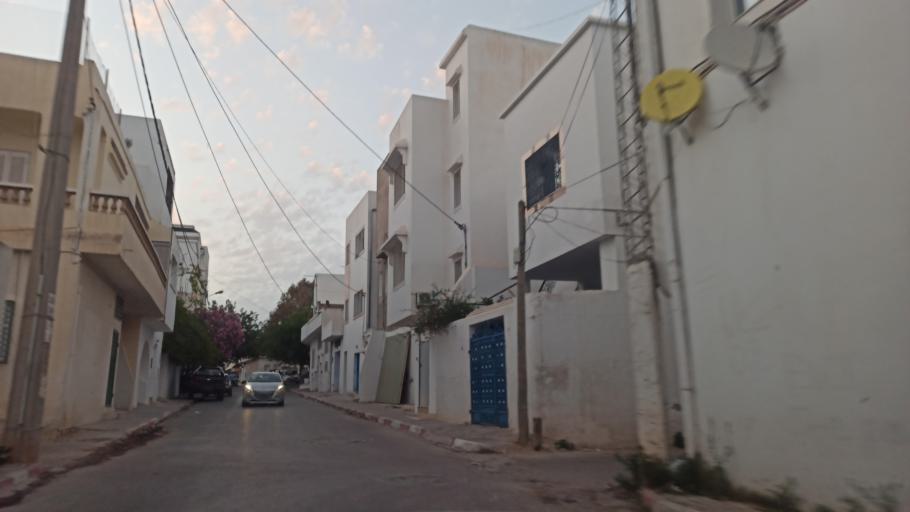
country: TN
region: Nabul
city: Al Hammamat
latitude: 36.4044
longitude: 10.6208
